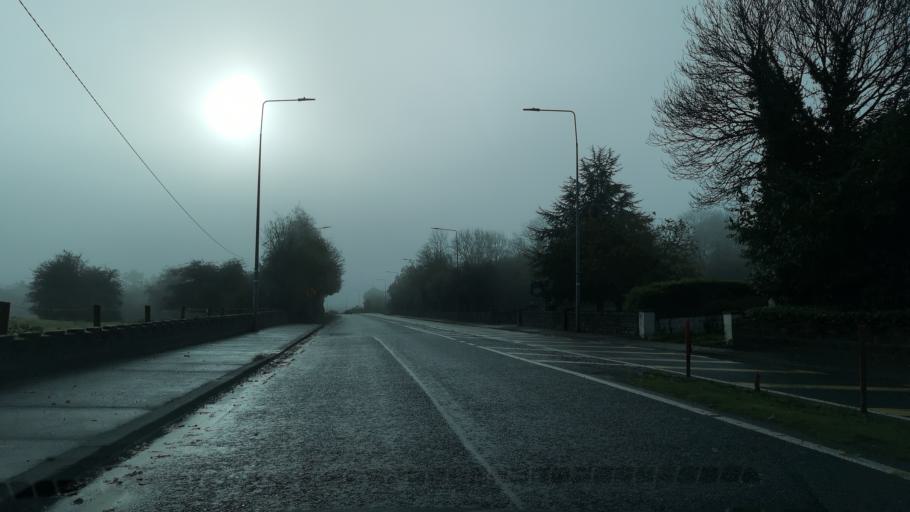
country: IE
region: Leinster
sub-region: An Iarmhi
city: Athlone
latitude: 53.4105
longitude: -7.8919
